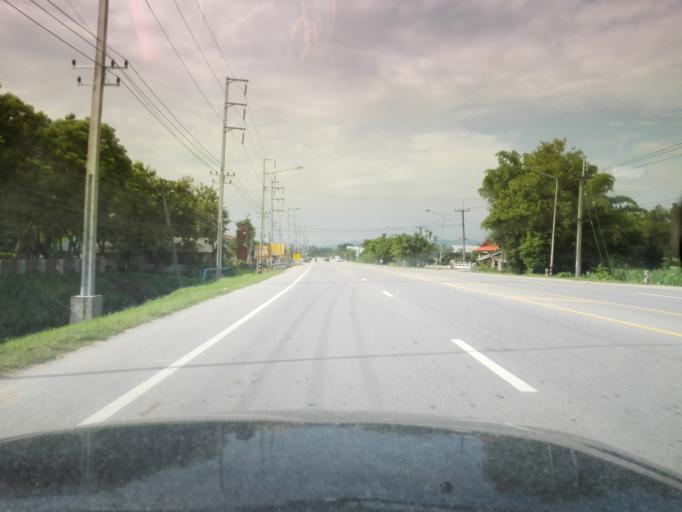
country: TH
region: Tak
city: Mae Sot
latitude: 16.7504
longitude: 98.5810
